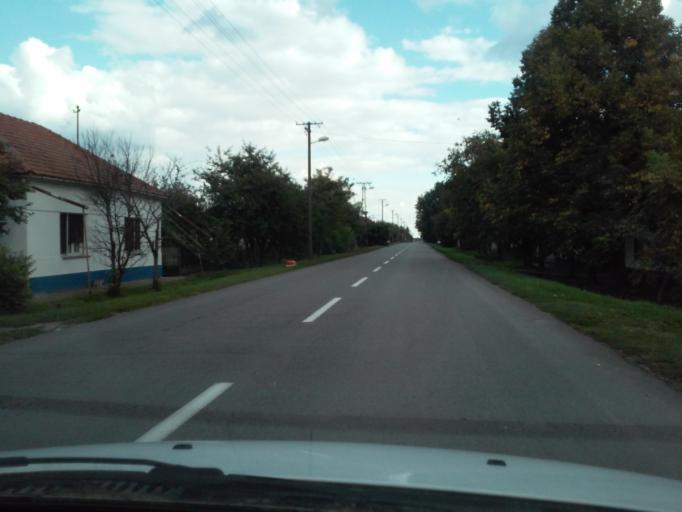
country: RS
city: Sajan
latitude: 45.8399
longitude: 20.2802
